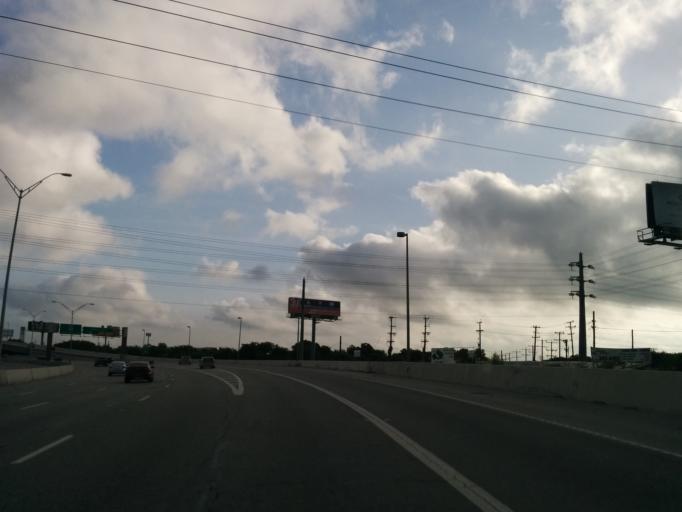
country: US
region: Texas
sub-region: Bexar County
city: Alamo Heights
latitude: 29.5103
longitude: -98.4763
